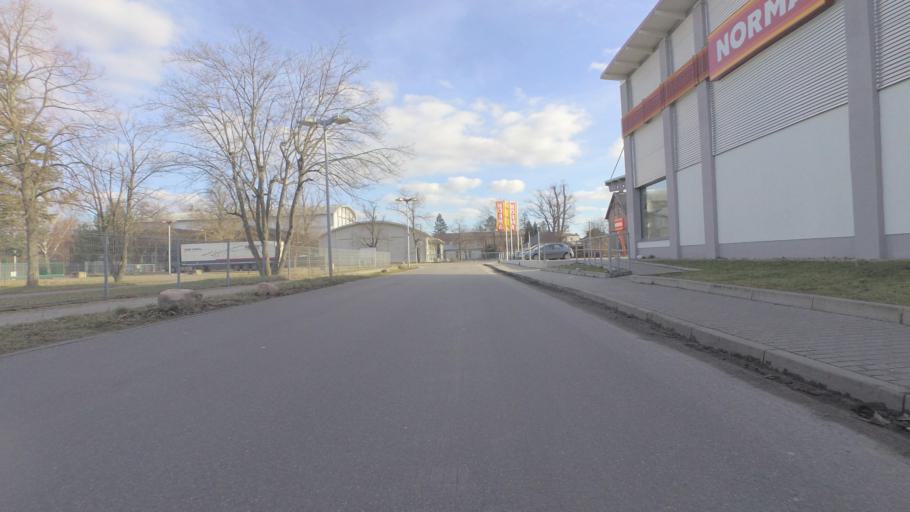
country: DE
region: Brandenburg
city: Trebbin
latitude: 52.2163
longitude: 13.2308
